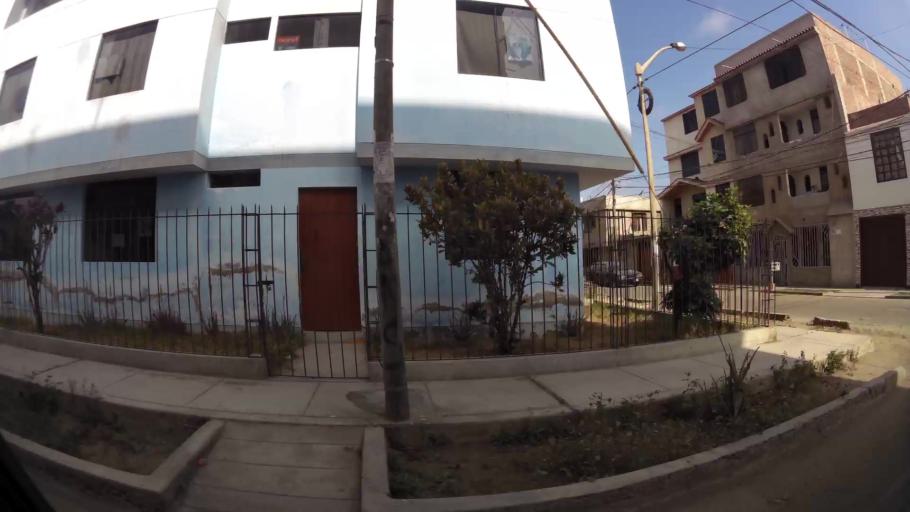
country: PE
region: La Libertad
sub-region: Provincia de Trujillo
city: Trujillo
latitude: -8.1217
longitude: -79.0168
